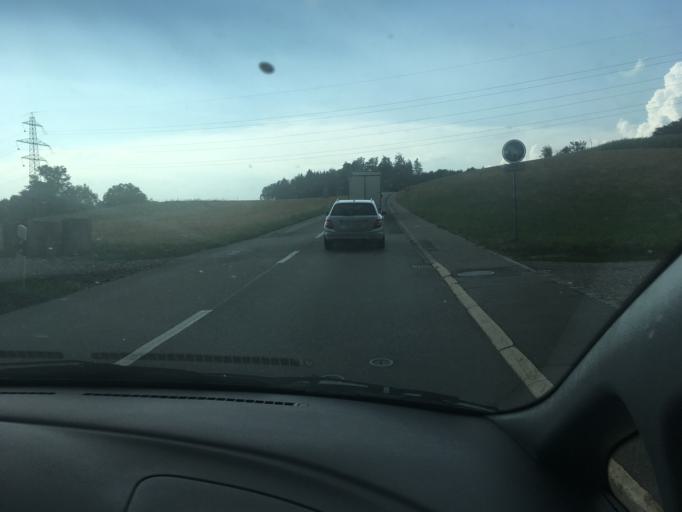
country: CH
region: Bern
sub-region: Bern-Mittelland District
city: Kirchlindach
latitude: 46.9972
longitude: 7.3915
